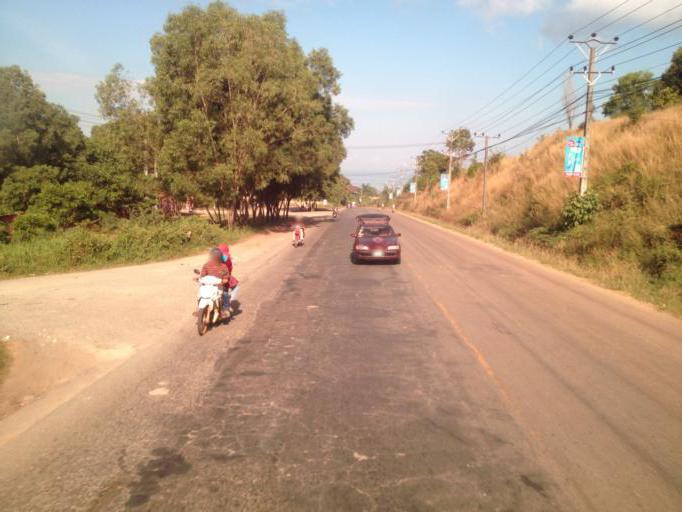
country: KH
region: Preah Sihanouk
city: Sihanoukville
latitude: 10.6389
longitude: 103.5305
